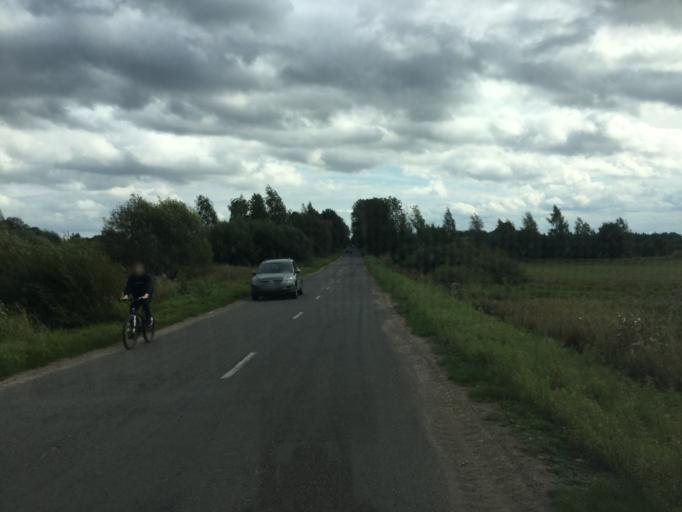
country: BY
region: Vitebsk
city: Vitebsk
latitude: 55.1478
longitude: 30.2801
